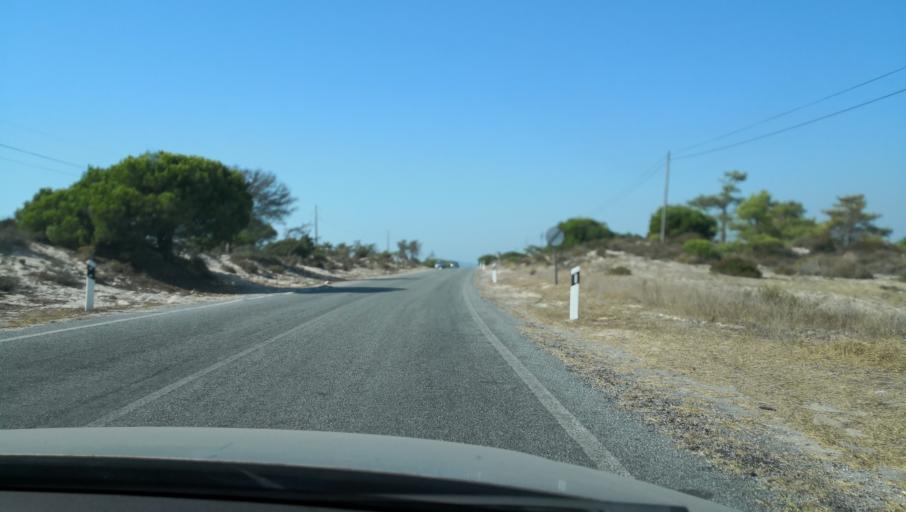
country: PT
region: Setubal
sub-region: Setubal
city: Setubal
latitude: 38.4200
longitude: -8.8204
